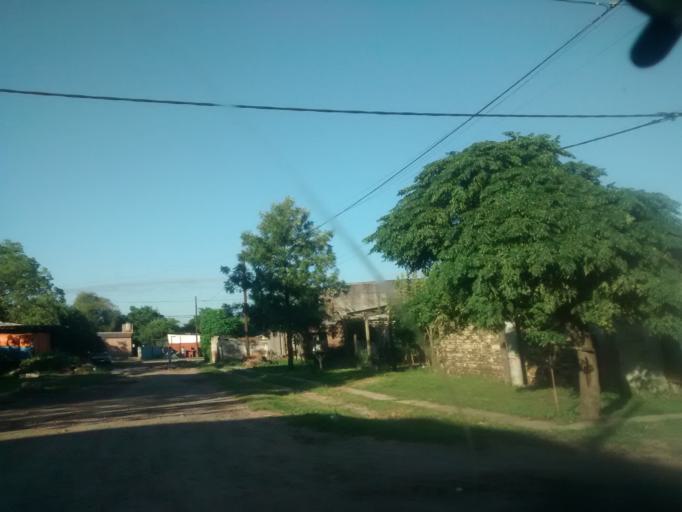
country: AR
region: Chaco
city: Resistencia
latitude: -27.4460
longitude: -59.0076
